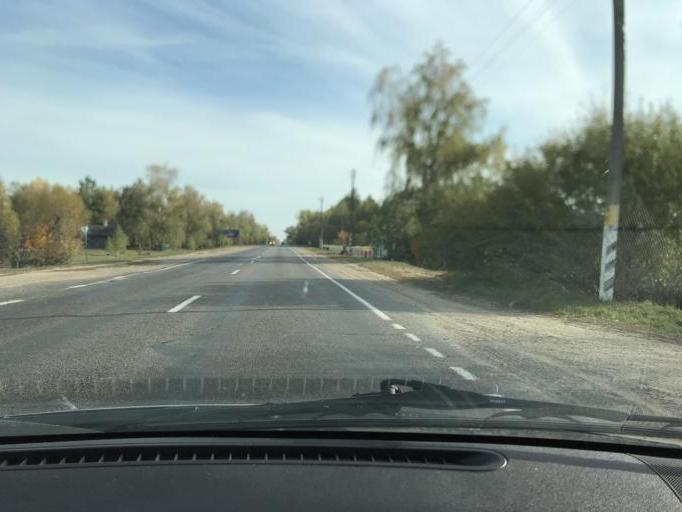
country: BY
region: Brest
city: Lahishyn
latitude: 52.2320
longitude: 26.0159
